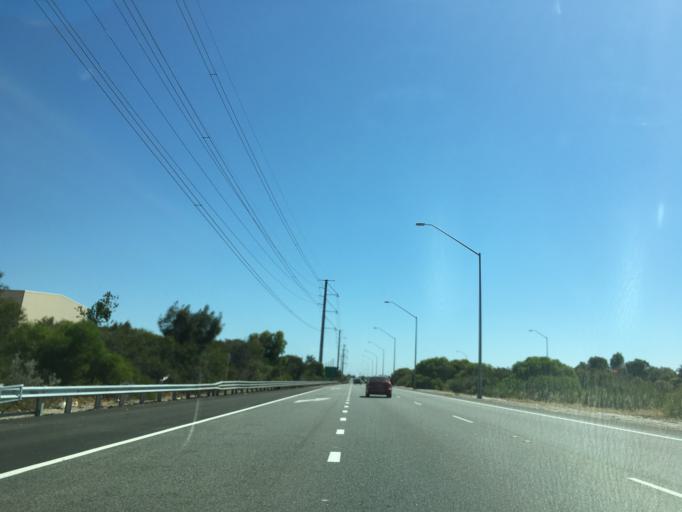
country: AU
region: Western Australia
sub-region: Canning
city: Willetton
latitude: -32.0603
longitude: 115.9011
